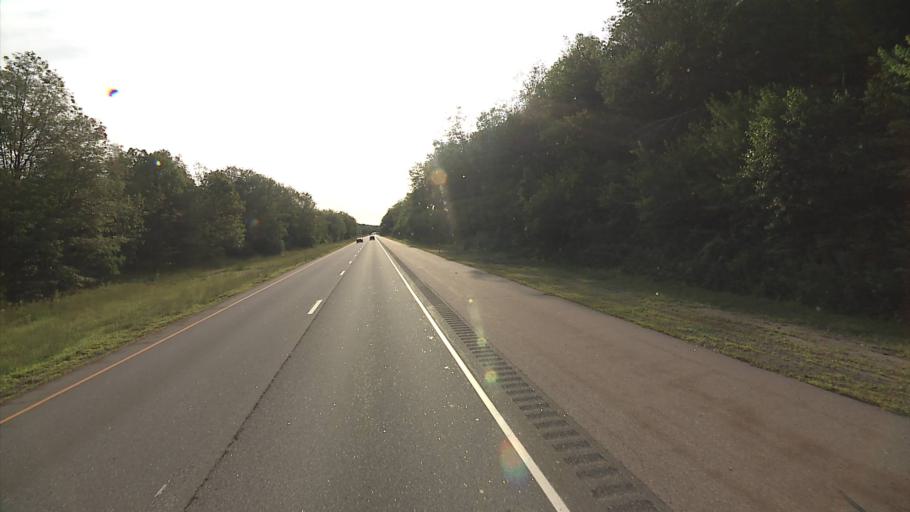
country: US
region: Connecticut
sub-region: New London County
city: Colchester
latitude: 41.5682
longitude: -72.2205
